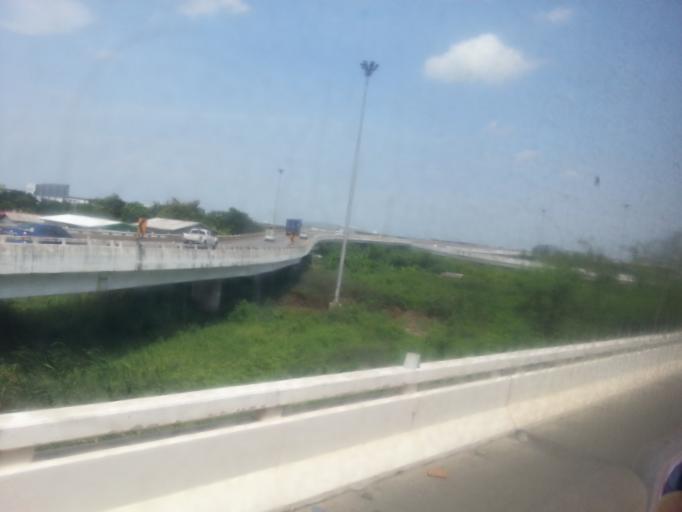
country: TH
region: Bangkok
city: Lat Krabang
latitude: 13.7196
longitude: 100.7468
